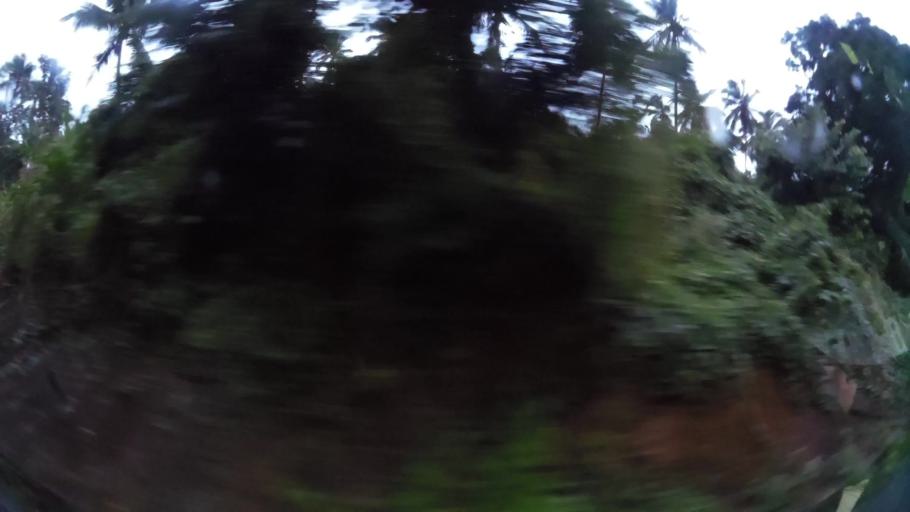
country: DM
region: Saint Andrew
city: Wesley
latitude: 15.5564
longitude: -61.3073
